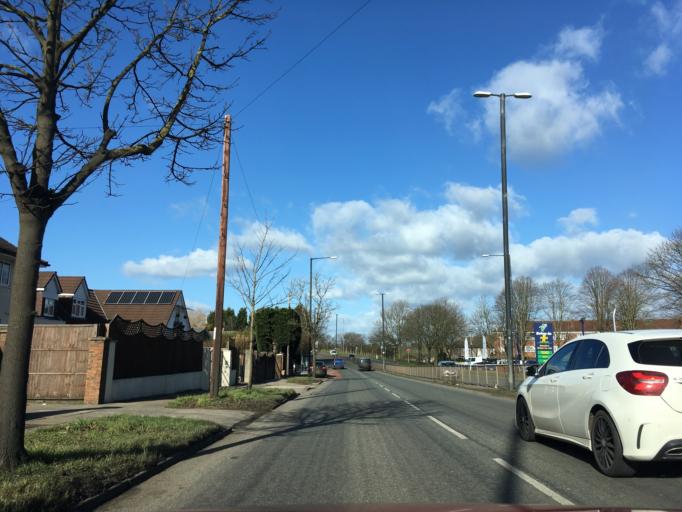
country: GB
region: England
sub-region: Bristol
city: Bristol
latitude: 51.5123
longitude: -2.6197
